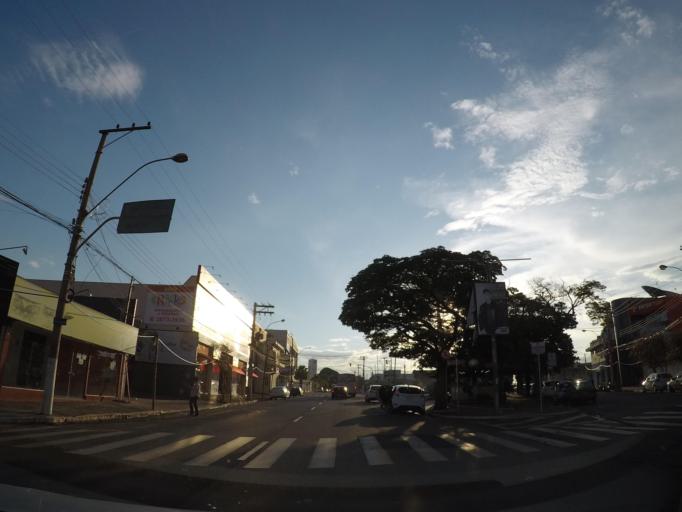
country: BR
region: Sao Paulo
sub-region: Sumare
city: Sumare
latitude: -22.8249
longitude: -47.2690
